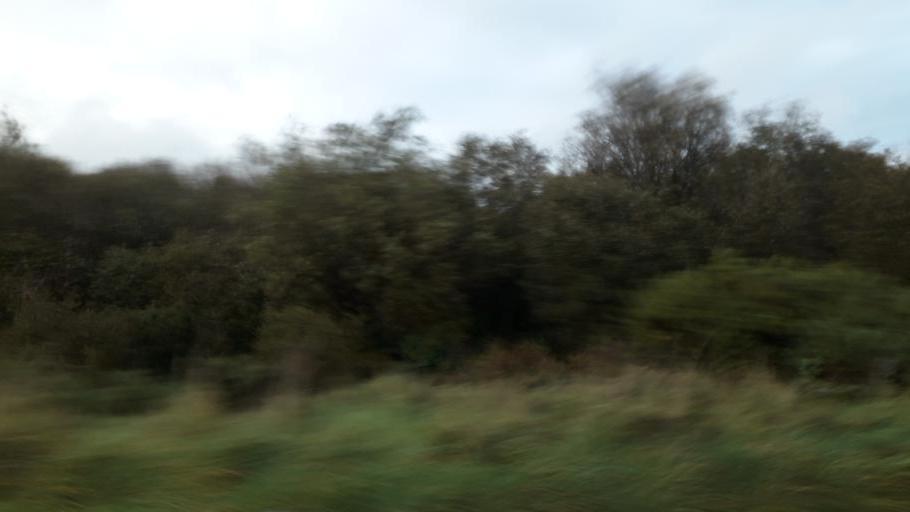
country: IE
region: Leinster
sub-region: An Longfort
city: Lanesborough
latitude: 53.7602
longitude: -7.9920
